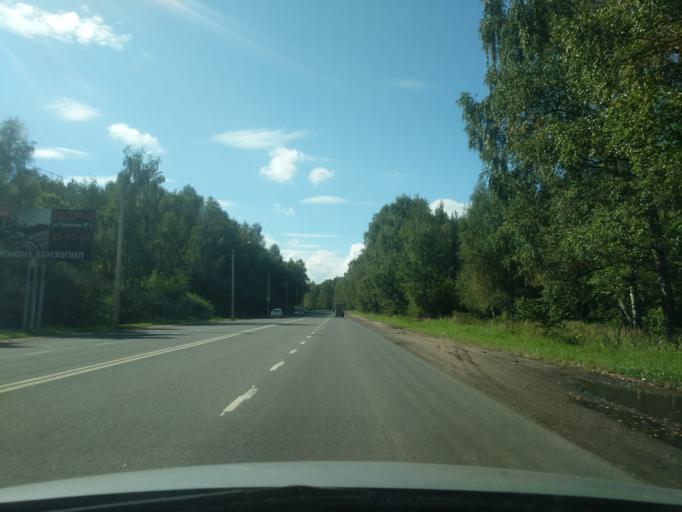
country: RU
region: Kostroma
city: Oktyabr'skiy
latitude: 57.7836
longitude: 41.0147
